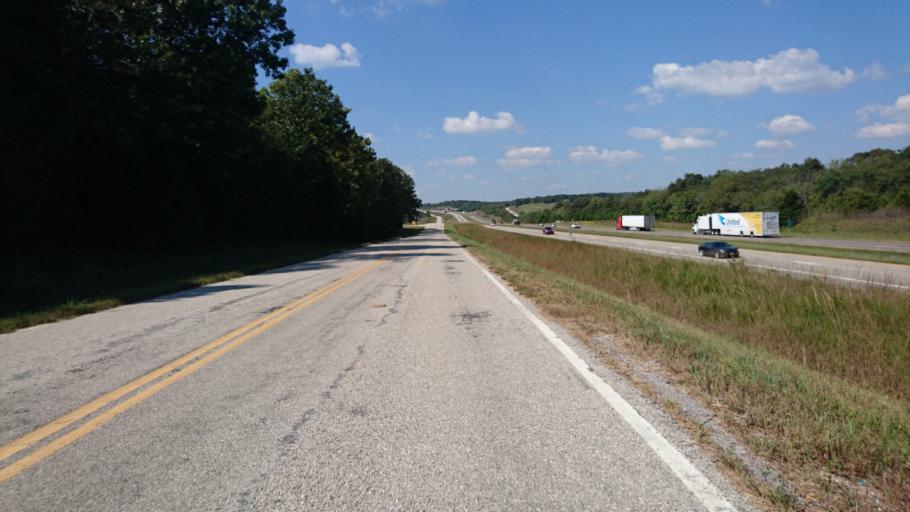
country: US
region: Missouri
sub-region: Pulaski County
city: Richland
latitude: 37.7575
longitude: -92.4606
